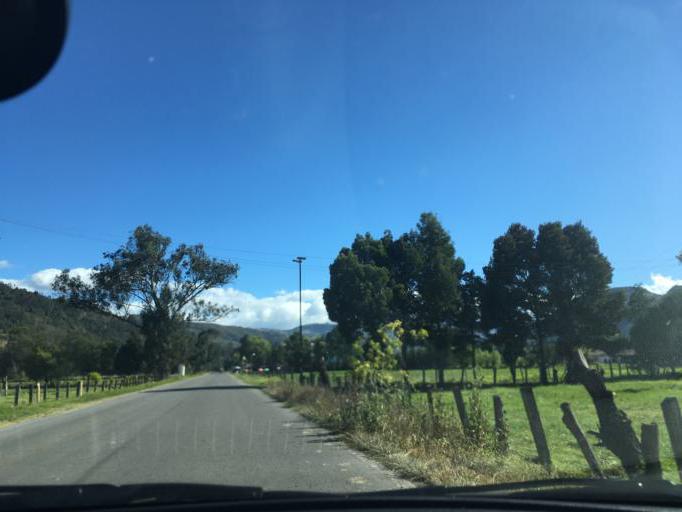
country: CO
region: Boyaca
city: Firavitoba
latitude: 5.6328
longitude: -72.9856
